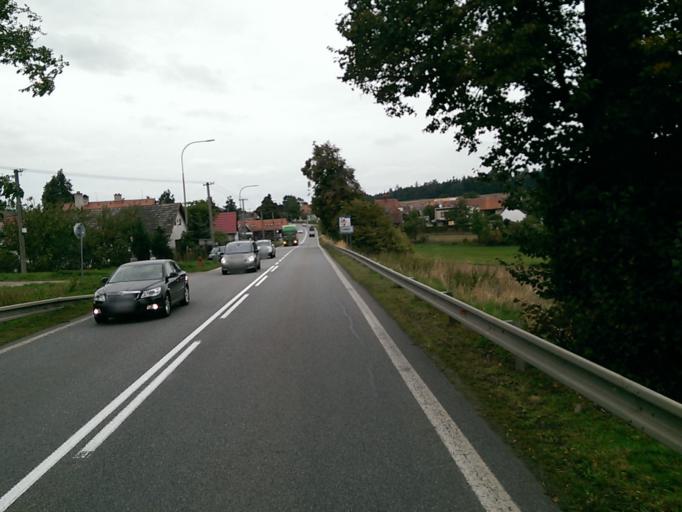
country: CZ
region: Vysocina
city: Zeletava
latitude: 49.1223
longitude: 15.7015
